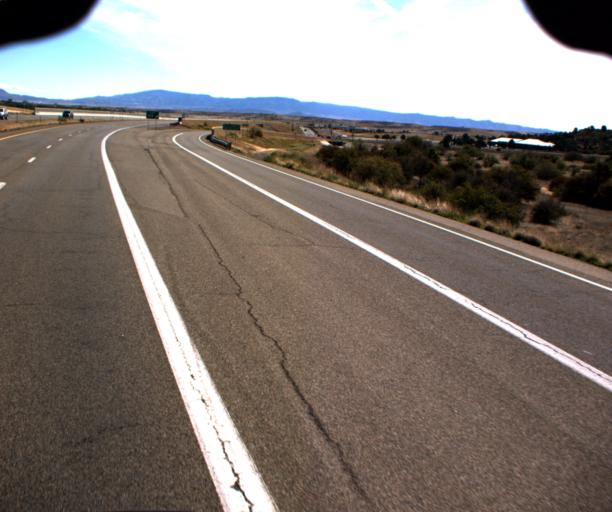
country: US
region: Arizona
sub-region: Yavapai County
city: Prescott
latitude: 34.6307
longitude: -112.4334
